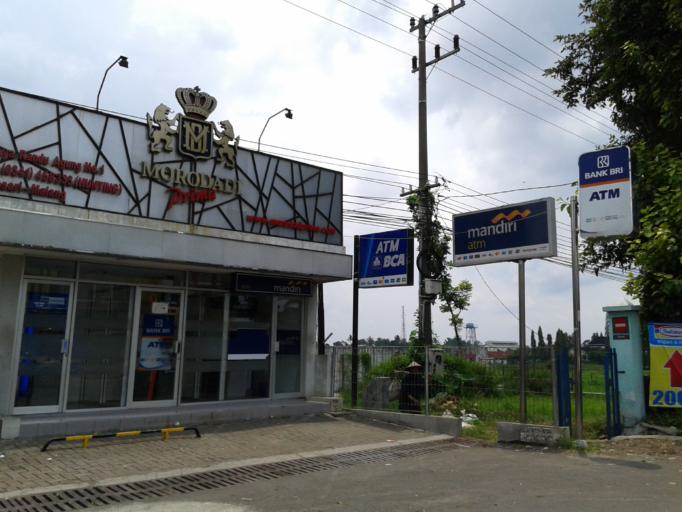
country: ID
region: East Java
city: Lawang
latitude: -7.8634
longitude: 112.6851
